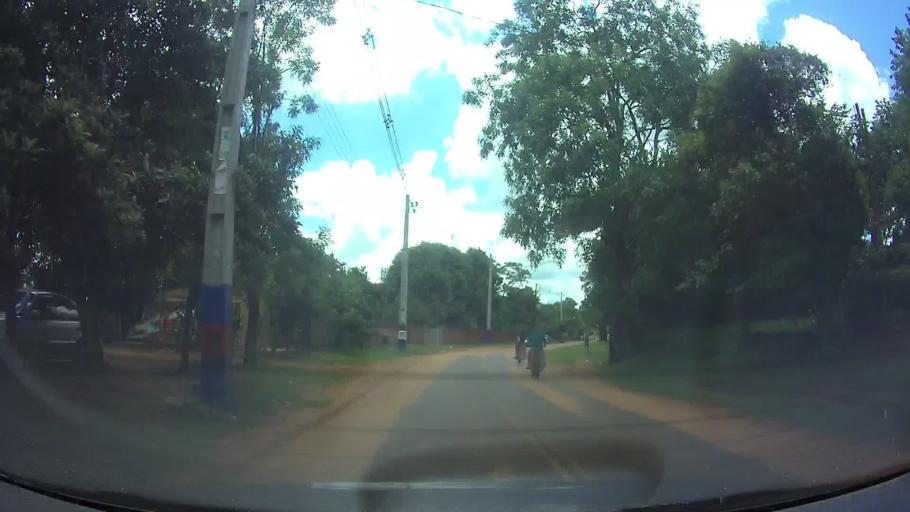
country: PY
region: Central
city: Capiata
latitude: -25.3314
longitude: -57.4218
